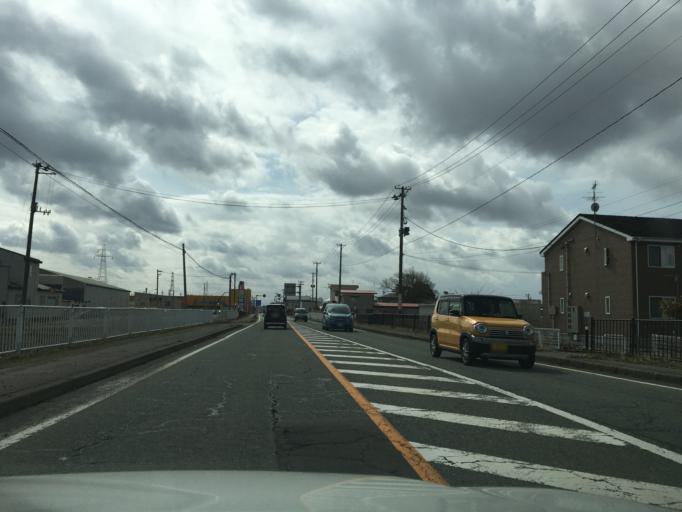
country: JP
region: Akita
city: Tenno
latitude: 39.9484
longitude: 140.0834
